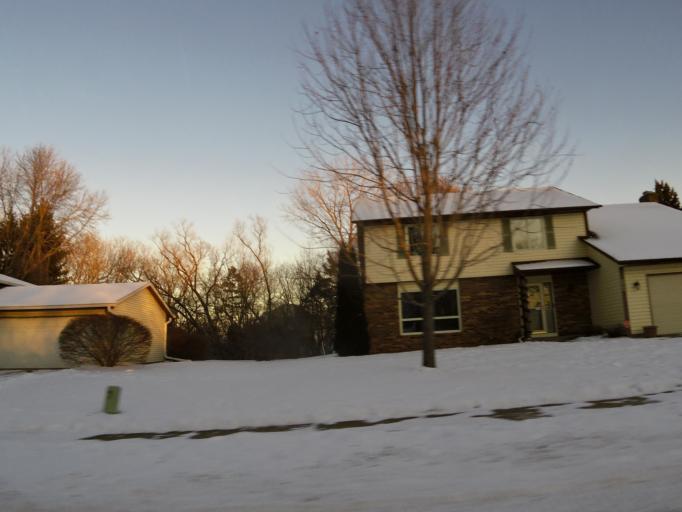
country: US
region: Minnesota
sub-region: Washington County
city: Stillwater
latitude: 45.0545
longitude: -92.8390
